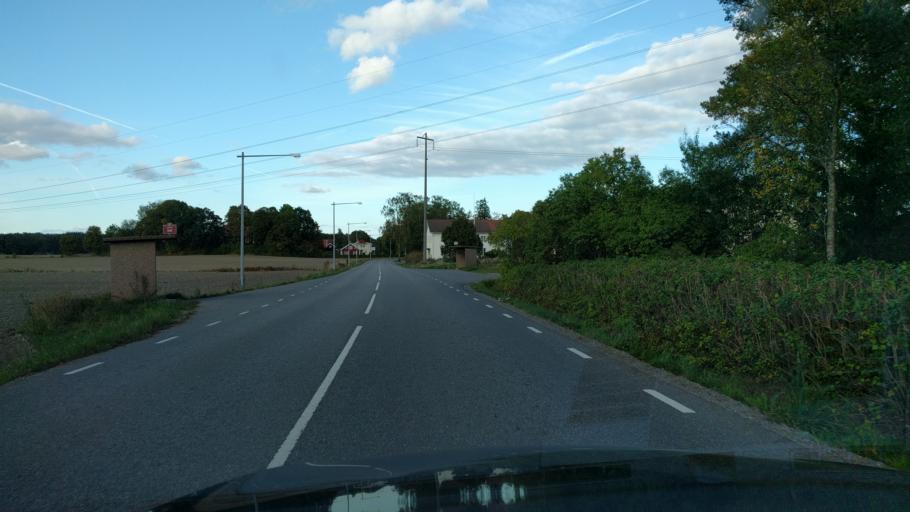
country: SE
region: Uppsala
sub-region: Tierps Kommun
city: Orbyhus
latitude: 60.1563
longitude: 17.5944
